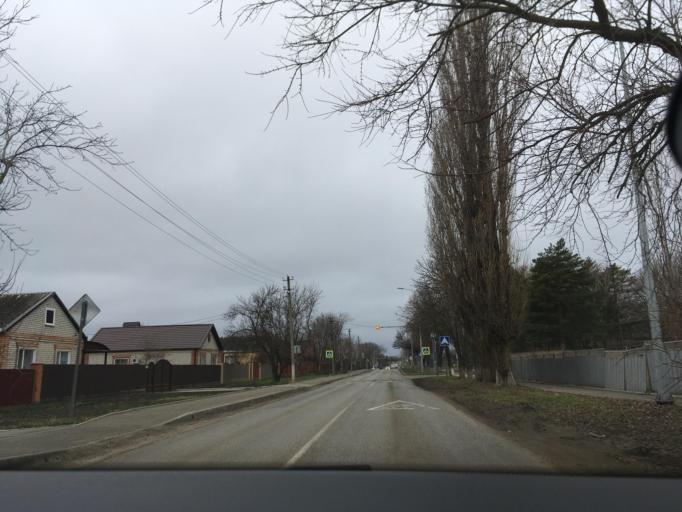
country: RU
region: Krasnodarskiy
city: Kushchevskaya
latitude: 46.5772
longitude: 39.6363
